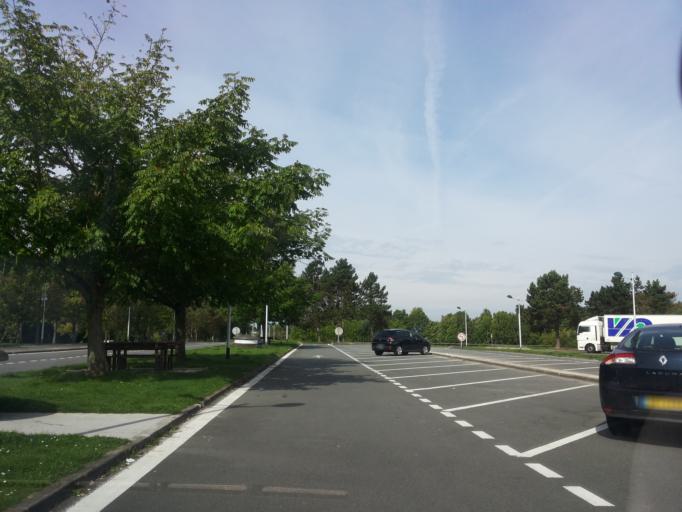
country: FR
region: Nord-Pas-de-Calais
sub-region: Departement du Pas-de-Calais
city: Souchez
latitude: 50.4051
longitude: 2.7439
